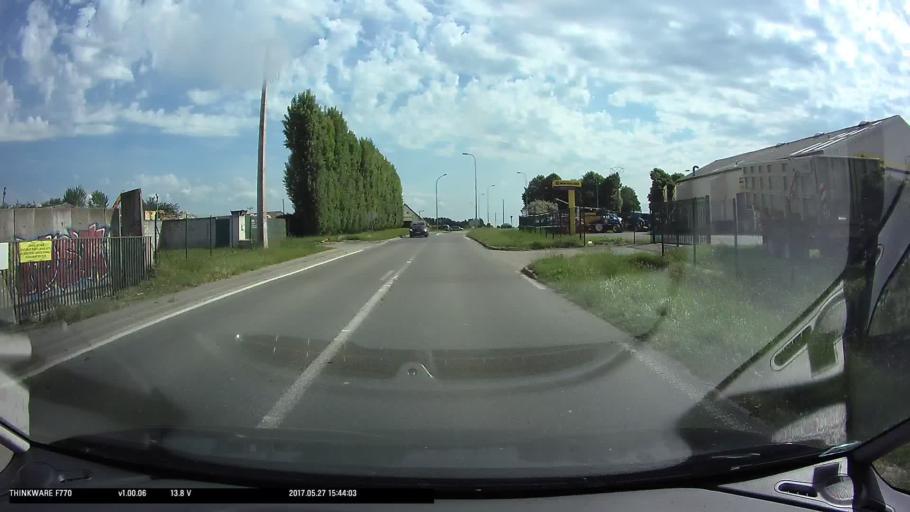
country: FR
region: Ile-de-France
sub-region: Departement du Val-d'Oise
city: Chars
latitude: 49.1965
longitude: 1.8800
